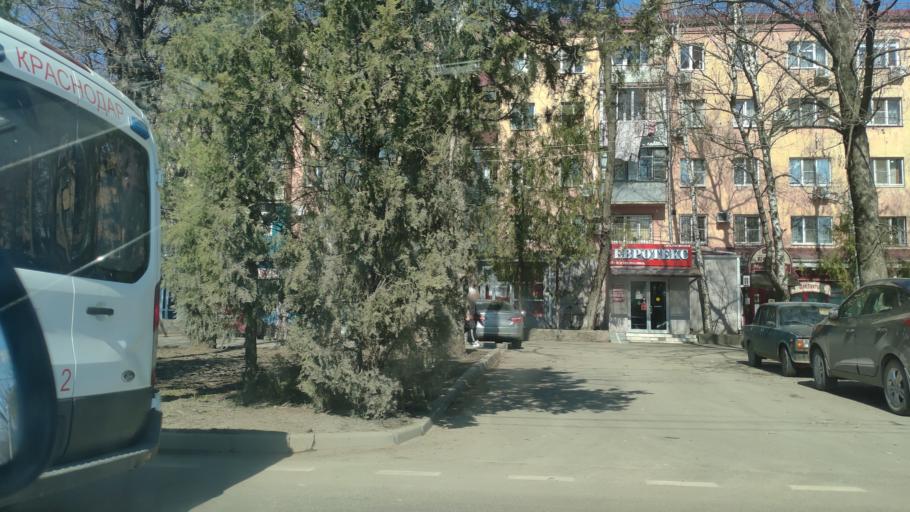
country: RU
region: Krasnodarskiy
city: Krasnodar
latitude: 45.0556
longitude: 39.0109
